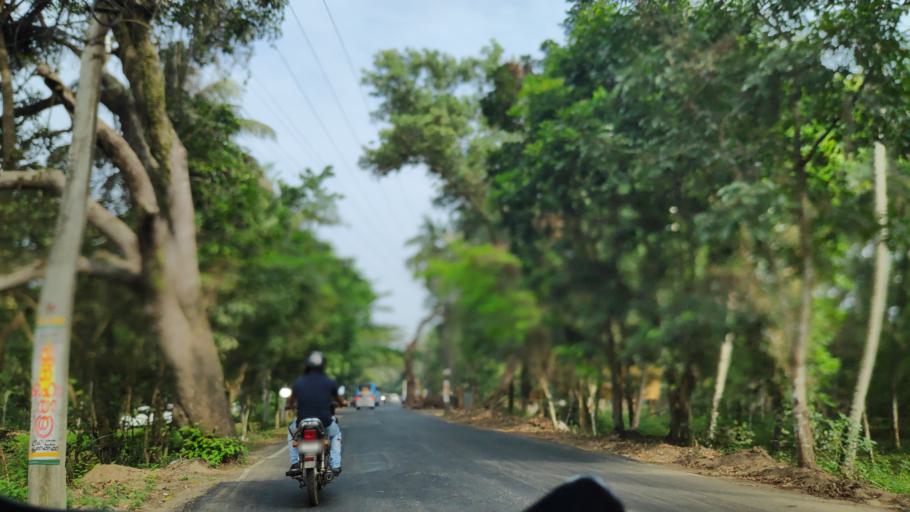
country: IN
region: Kerala
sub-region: Alappuzha
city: Kutiatodu
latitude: 9.7748
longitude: 76.3613
